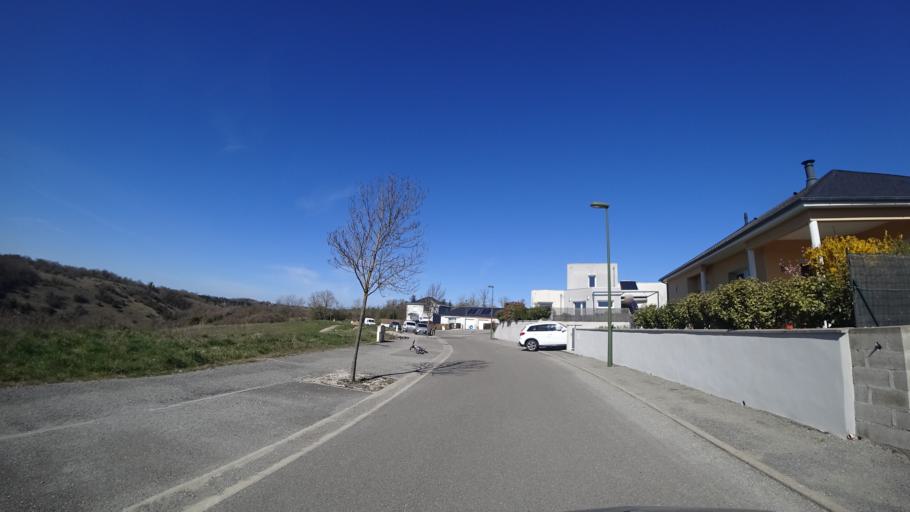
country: FR
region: Midi-Pyrenees
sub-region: Departement de l'Aveyron
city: Rodez
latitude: 44.3818
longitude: 2.5685
